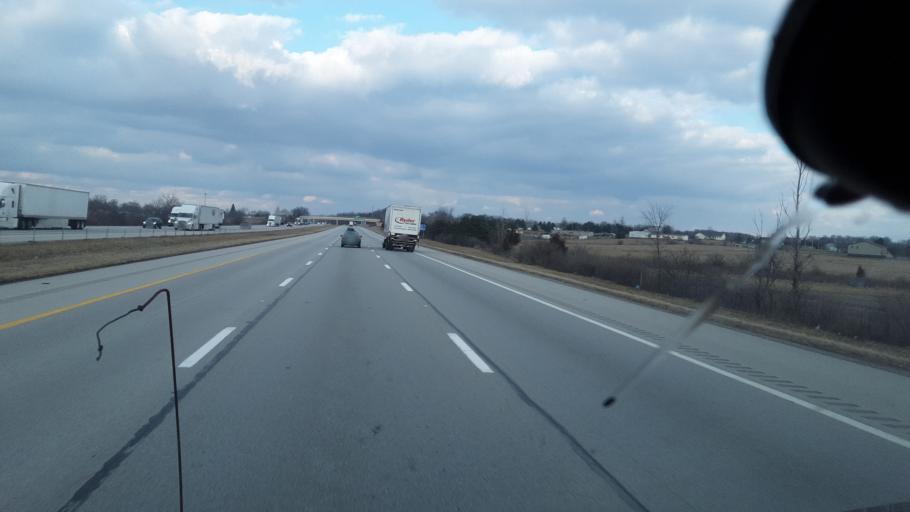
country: US
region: Ohio
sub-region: Clark County
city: Lisbon
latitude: 39.9123
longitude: -83.7022
